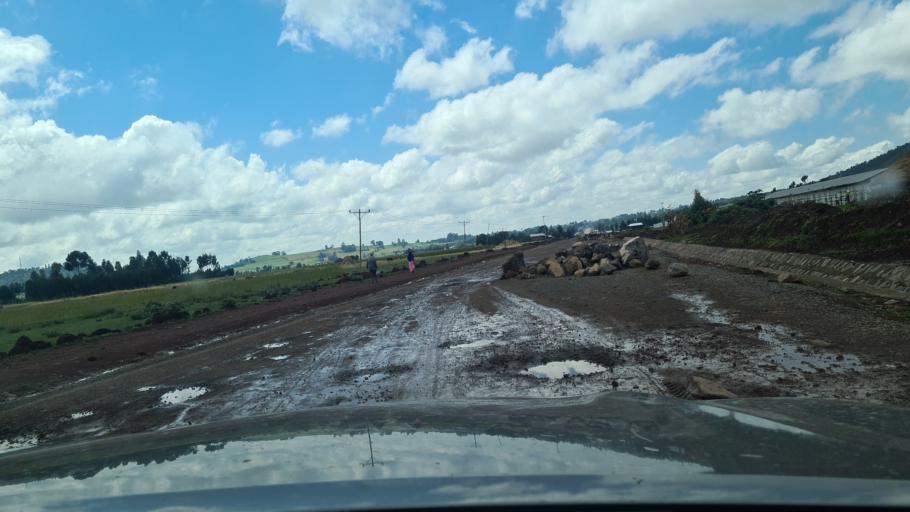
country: ET
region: Oromiya
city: Huruta
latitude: 8.0828
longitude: 39.5430
